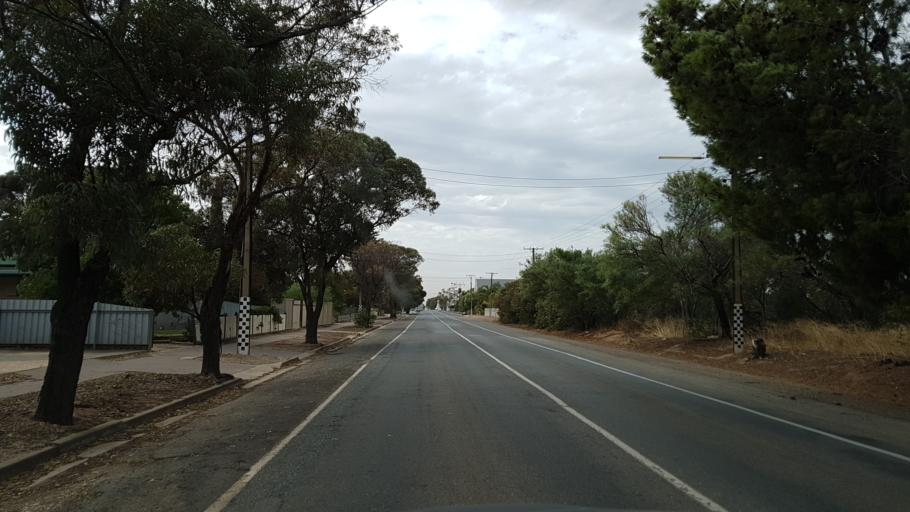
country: AU
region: South Australia
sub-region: Mallala
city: Mallala
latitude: -34.4358
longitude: 138.5055
